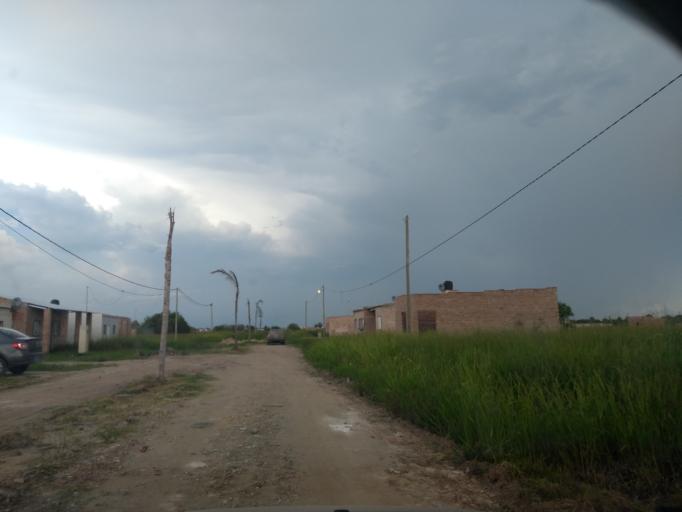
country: AR
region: Chaco
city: Resistencia
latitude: -27.4673
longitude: -59.0292
